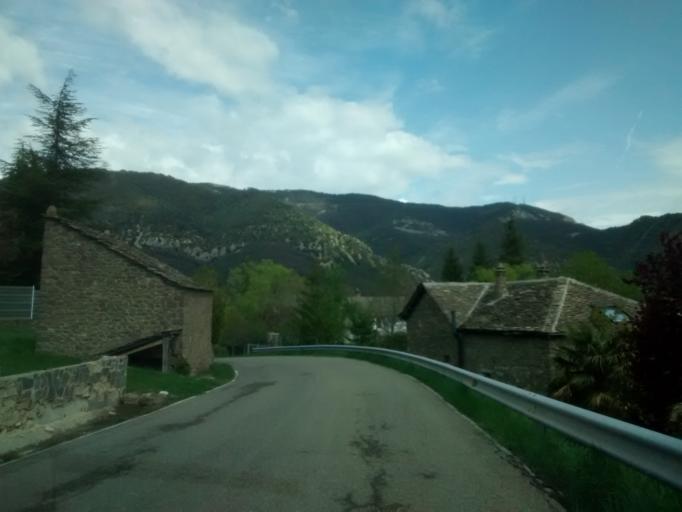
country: ES
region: Aragon
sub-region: Provincia de Huesca
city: Arguis
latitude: 42.3156
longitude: -0.4393
